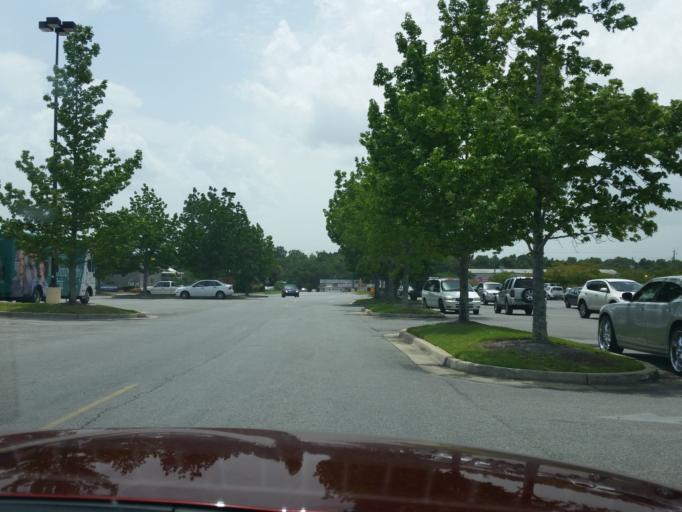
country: US
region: Florida
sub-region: Escambia County
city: Ensley
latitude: 30.5289
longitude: -87.2734
